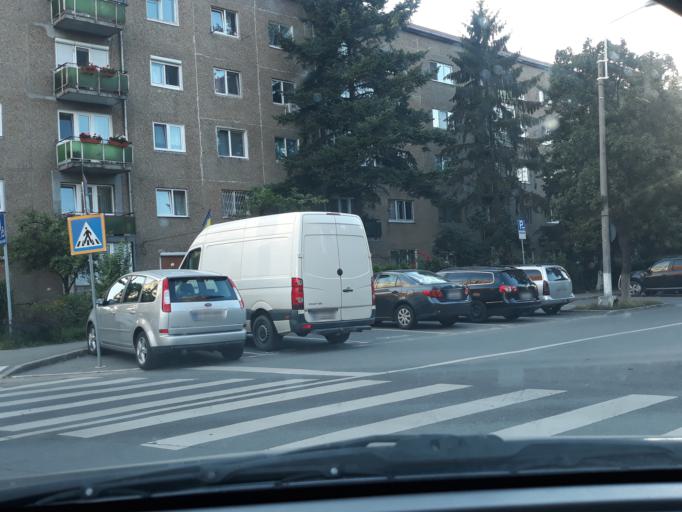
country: RO
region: Bihor
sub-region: Comuna Biharea
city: Oradea
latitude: 47.0792
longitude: 21.9171
